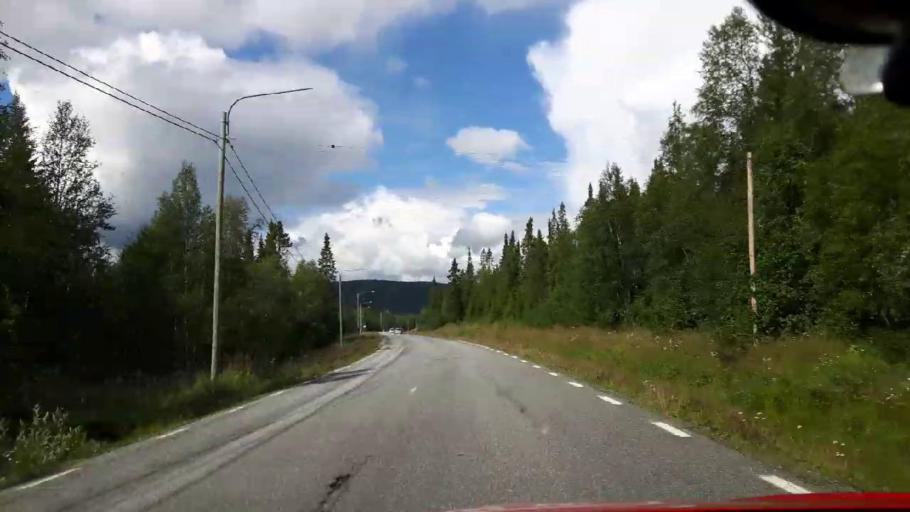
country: NO
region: Nordland
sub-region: Hattfjelldal
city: Hattfjelldal
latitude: 65.0629
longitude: 14.8704
